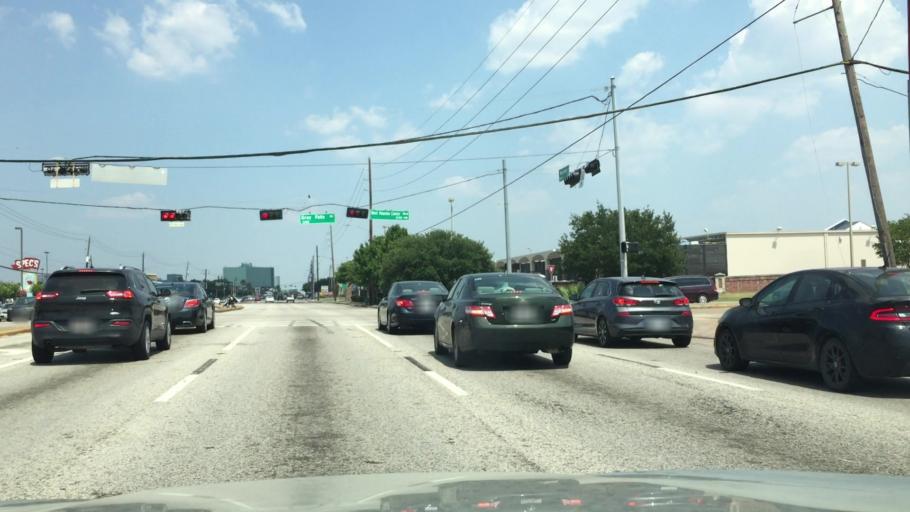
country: US
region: Texas
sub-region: Harris County
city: Bunker Hill Village
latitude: 29.7363
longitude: -95.5930
